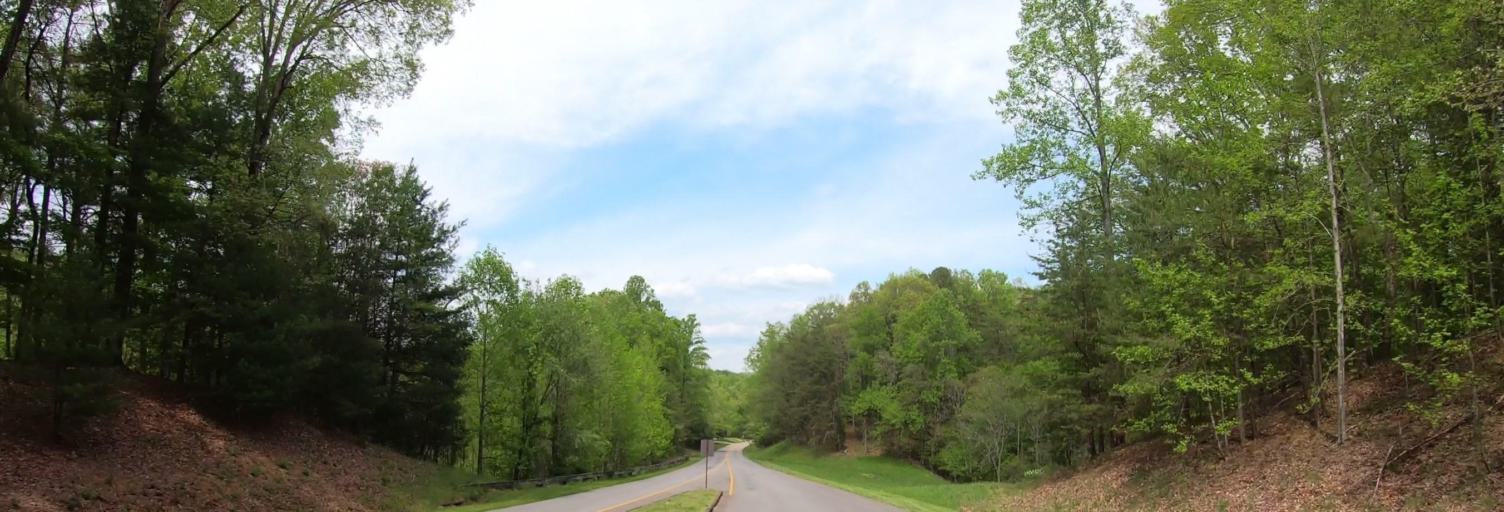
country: US
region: Virginia
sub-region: Roanoke County
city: Vinton
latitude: 37.2499
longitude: -79.8726
